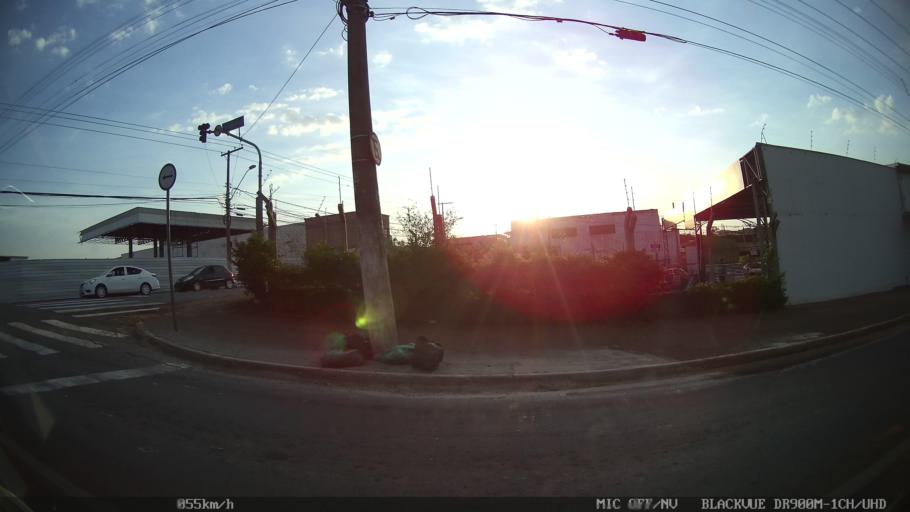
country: BR
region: Sao Paulo
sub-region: Ribeirao Preto
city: Ribeirao Preto
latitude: -21.1528
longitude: -47.8095
